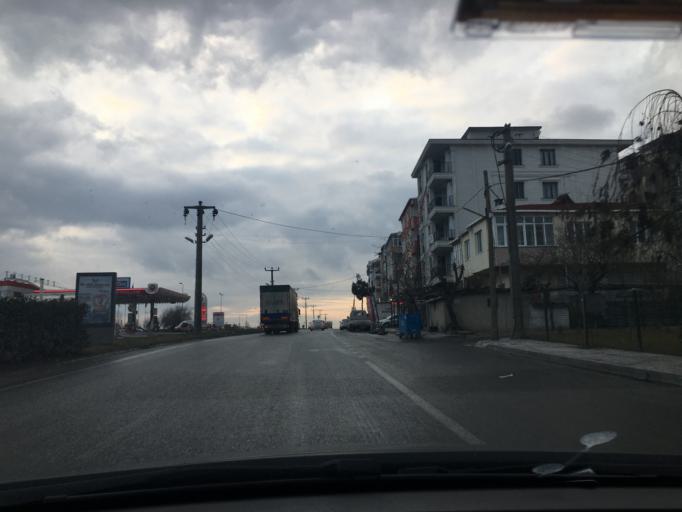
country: TR
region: Tekirdag
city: Cerkezkoey
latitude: 41.2792
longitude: 27.9854
